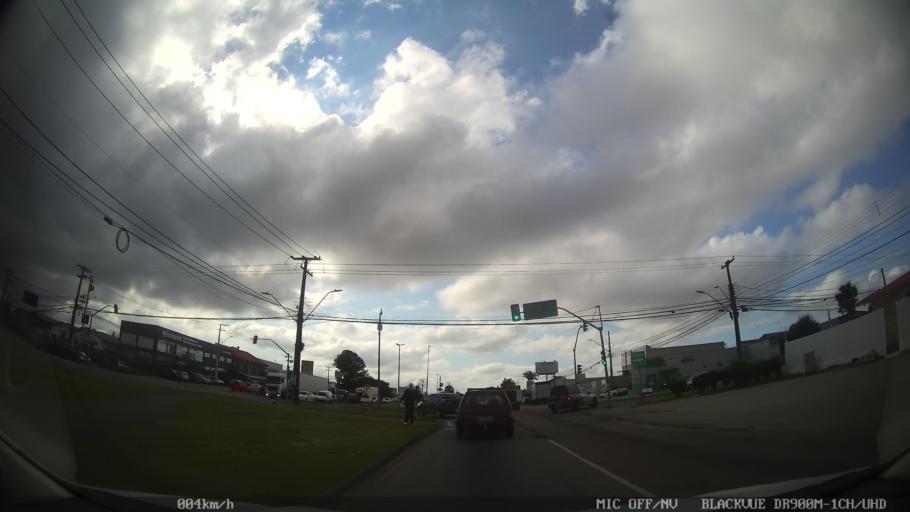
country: BR
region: Parana
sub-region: Pinhais
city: Pinhais
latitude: -25.4240
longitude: -49.1914
